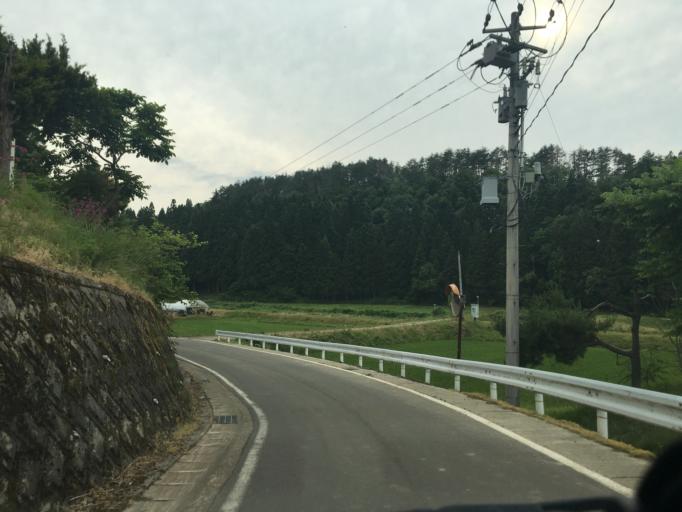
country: JP
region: Fukushima
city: Kitakata
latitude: 37.5057
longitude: 139.8031
